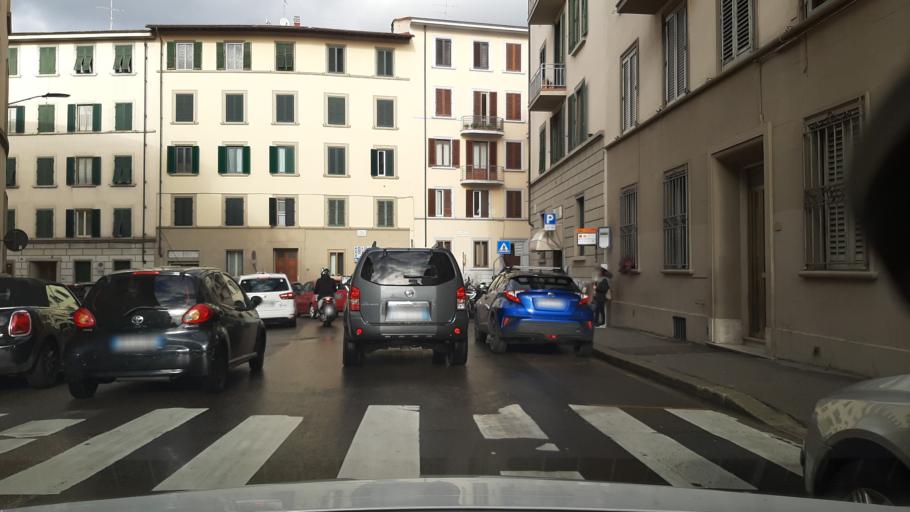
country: IT
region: Tuscany
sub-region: Province of Florence
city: Florence
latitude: 43.7946
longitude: 11.2453
